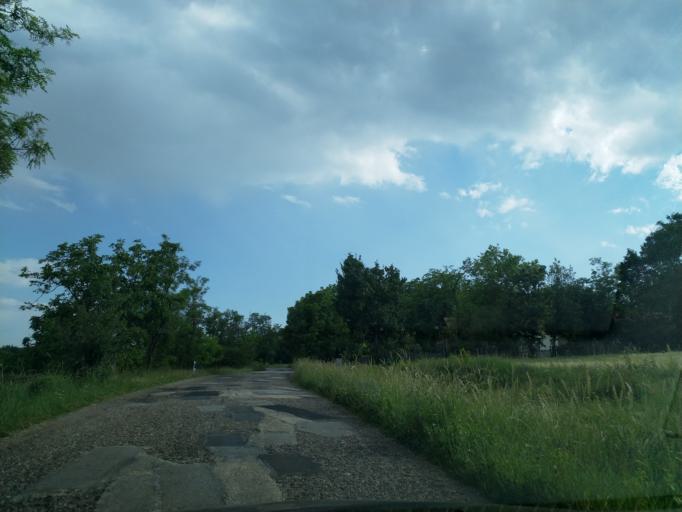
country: RS
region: Central Serbia
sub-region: Zajecarski Okrug
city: Boljevac
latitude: 43.9822
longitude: 21.9734
